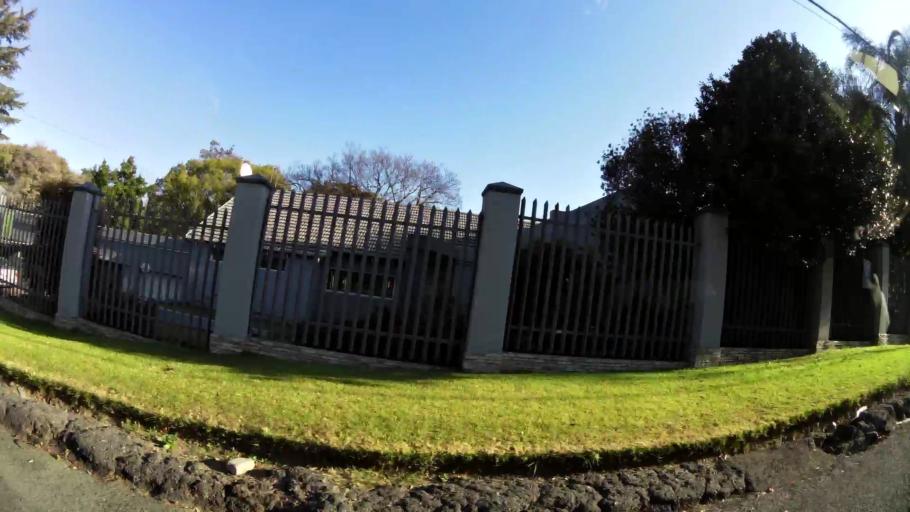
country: ZA
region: Gauteng
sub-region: City of Johannesburg Metropolitan Municipality
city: Johannesburg
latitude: -26.1301
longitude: 28.0778
